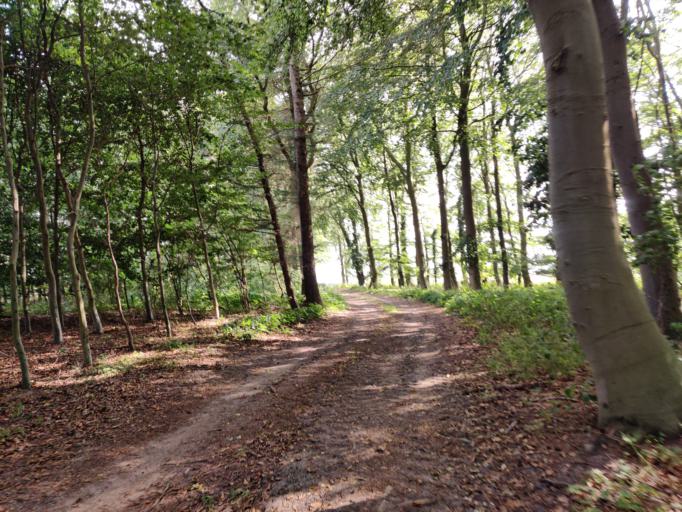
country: DK
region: Zealand
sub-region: Guldborgsund Kommune
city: Nykobing Falster
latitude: 54.6815
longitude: 11.9111
